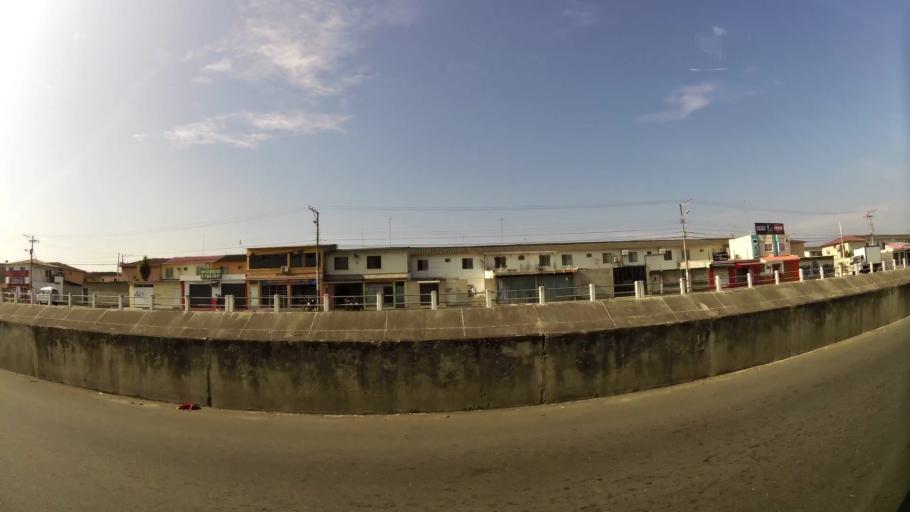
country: EC
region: Guayas
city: Eloy Alfaro
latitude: -2.0933
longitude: -79.9161
